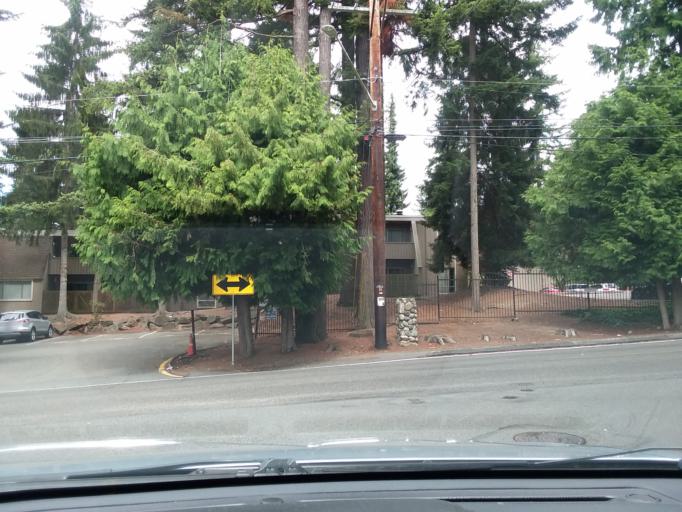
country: US
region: Washington
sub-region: Snohomish County
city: Alderwood Manor
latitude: 47.8355
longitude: -122.2979
